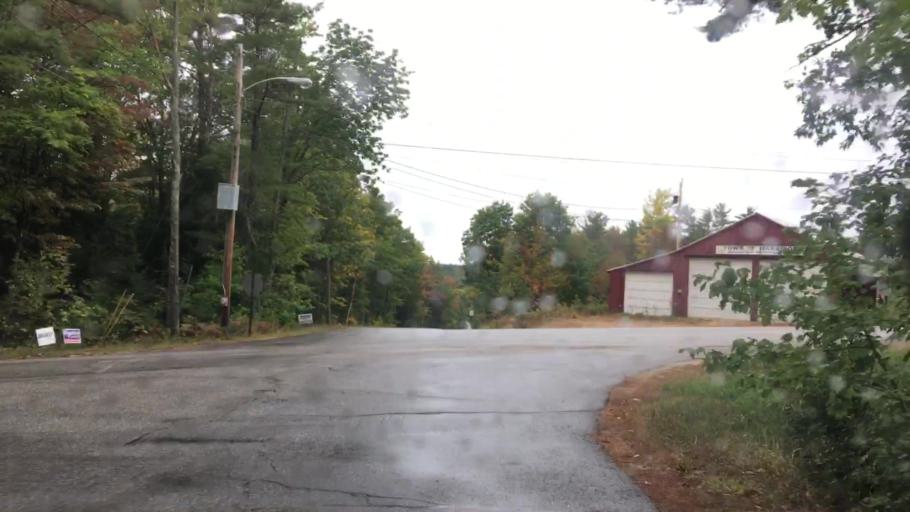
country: US
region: Maine
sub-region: Cumberland County
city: Harrison
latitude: 44.0783
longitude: -70.6414
